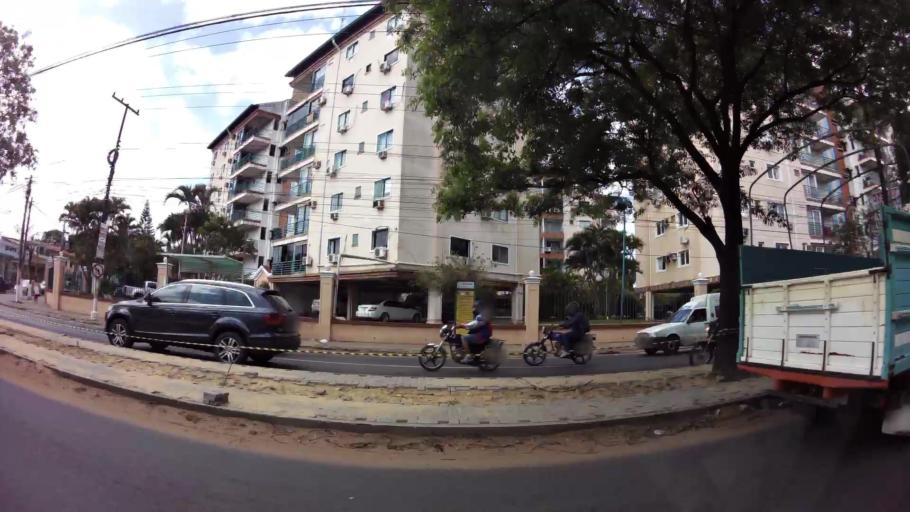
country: PY
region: Central
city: Fernando de la Mora
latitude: -25.3213
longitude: -57.5231
